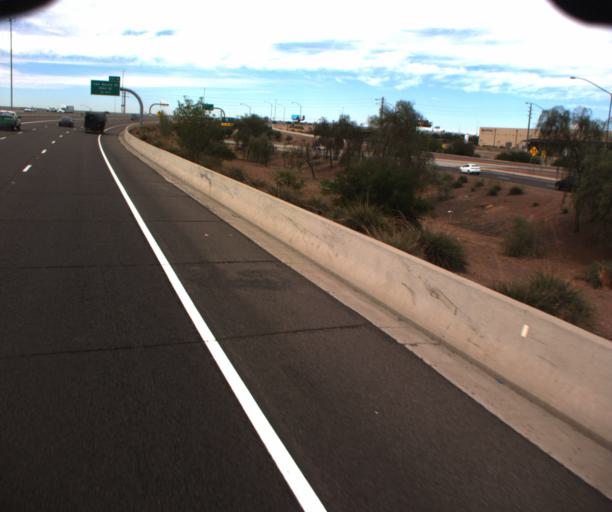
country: US
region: Arizona
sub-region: Maricopa County
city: Tempe Junction
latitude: 33.4387
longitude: -111.9639
